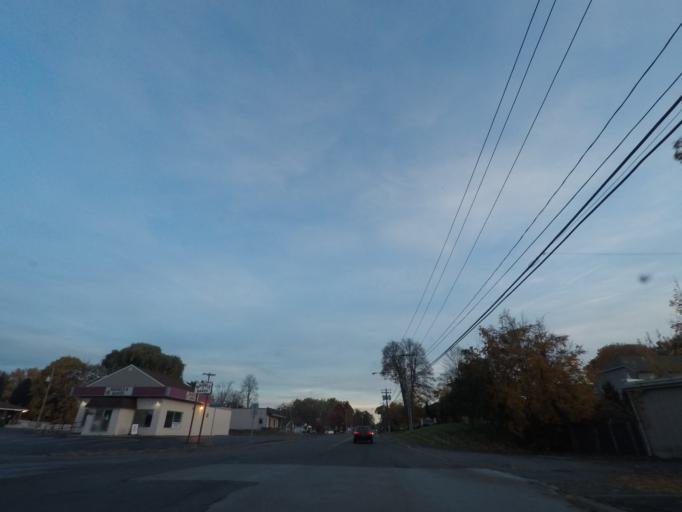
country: US
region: New York
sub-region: Schenectady County
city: Rotterdam
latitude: 42.7793
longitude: -73.9556
